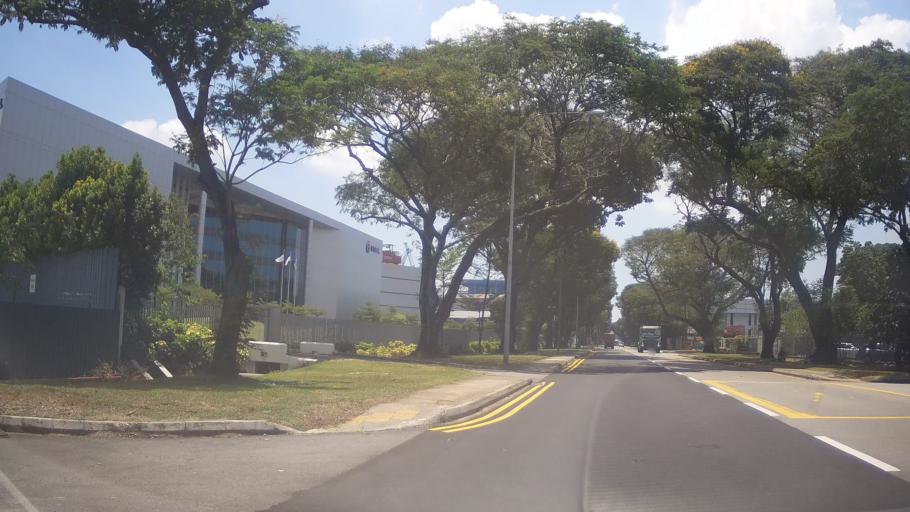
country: SG
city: Singapore
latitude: 1.3078
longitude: 103.6788
